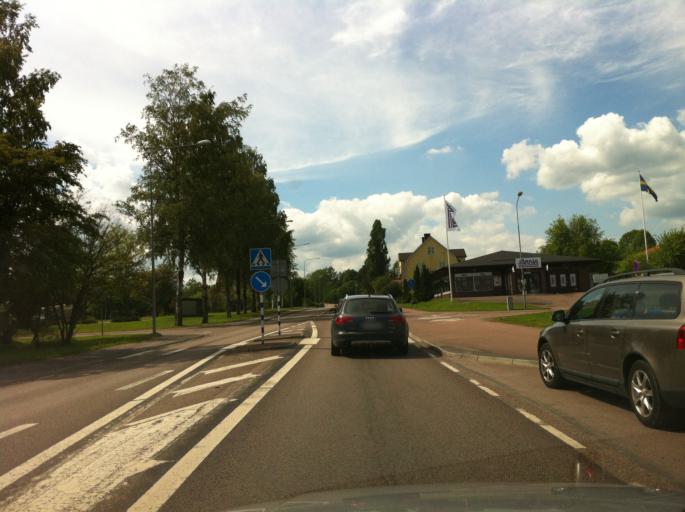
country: SE
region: Vaermland
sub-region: Sunne Kommun
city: Sunne
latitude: 59.8378
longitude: 13.1409
